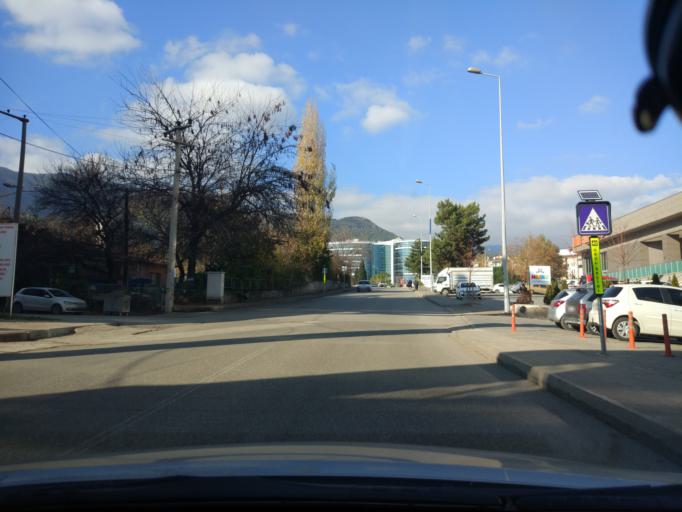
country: TR
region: Karabuk
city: Karabuk
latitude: 41.2052
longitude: 32.6206
